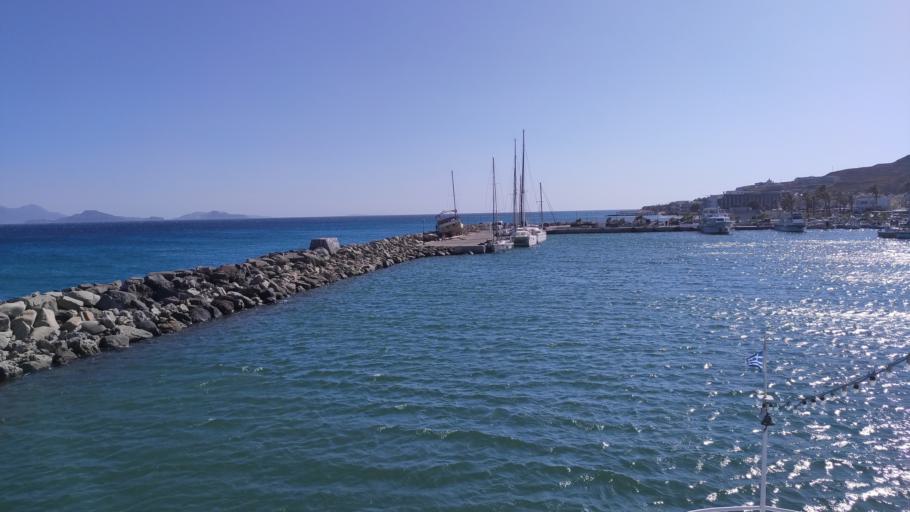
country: GR
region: South Aegean
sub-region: Nomos Dodekanisou
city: Kardamaina
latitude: 36.7823
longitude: 27.1462
